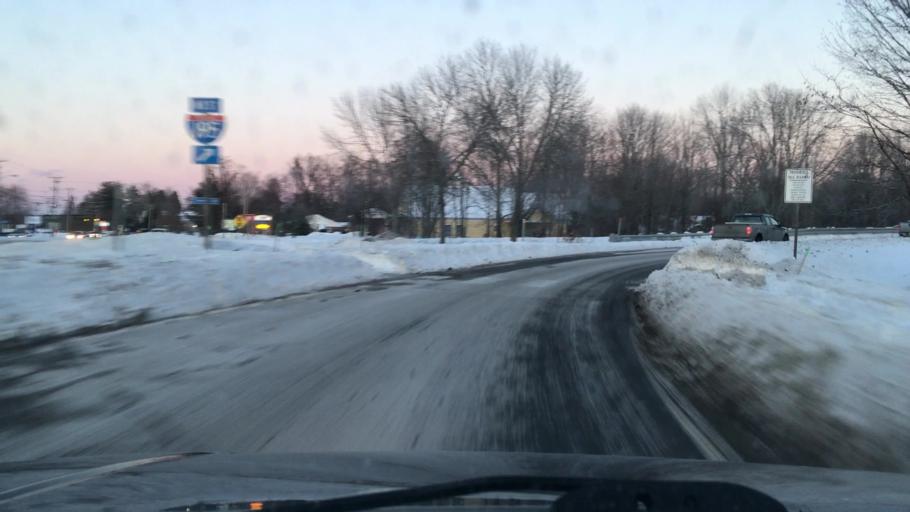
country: US
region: Maine
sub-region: York County
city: Saco
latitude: 43.5125
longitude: -70.4312
